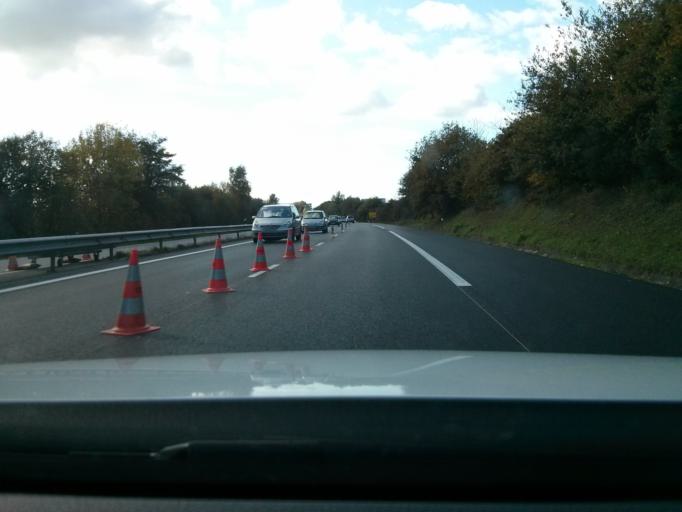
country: FR
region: Brittany
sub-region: Departement des Cotes-d'Armor
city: Plouer-sur-Rance
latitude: 48.5261
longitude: -2.0348
